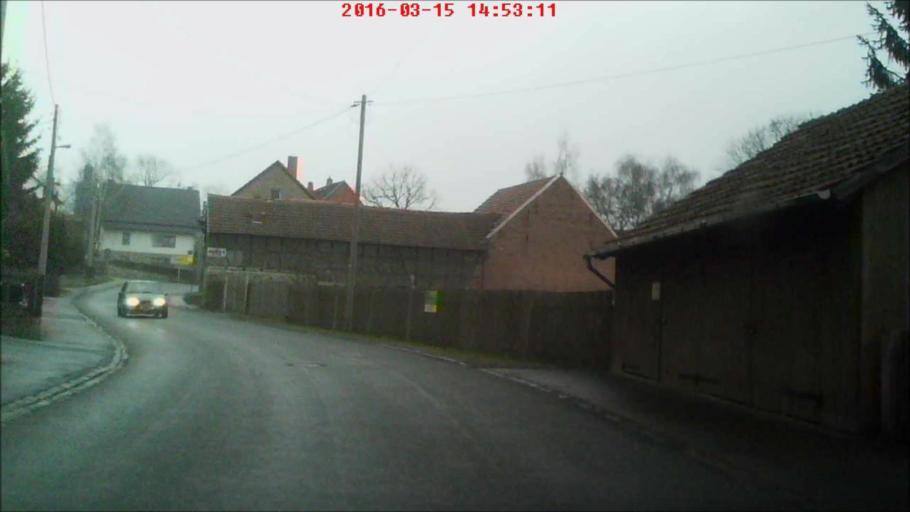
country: DE
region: Thuringia
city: Rockhausen
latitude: 50.9184
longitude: 11.0490
